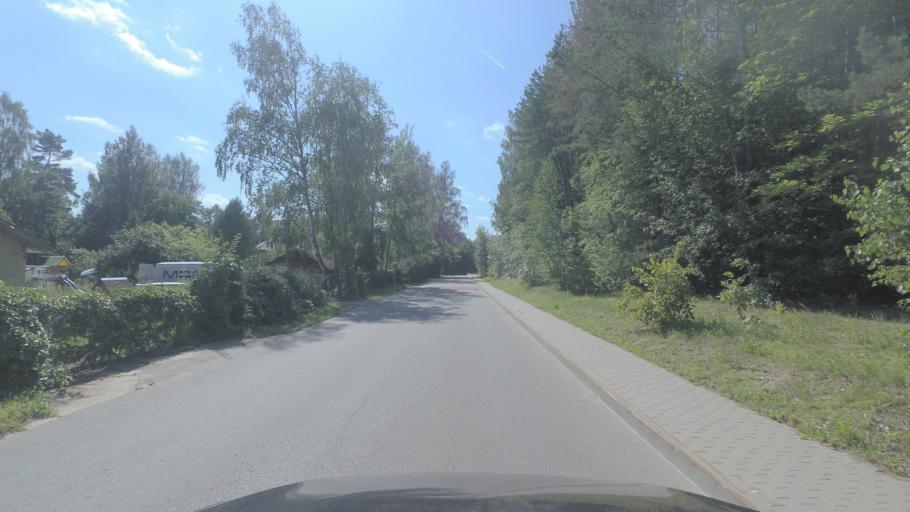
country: LT
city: Nemencine
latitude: 54.8539
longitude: 25.3776
